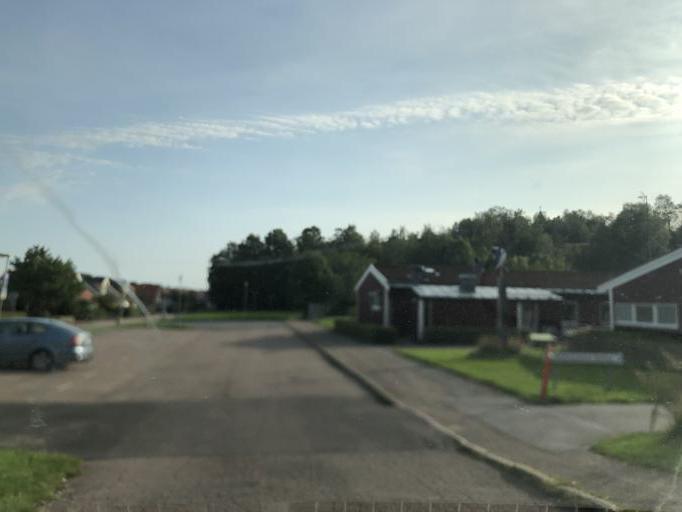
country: SE
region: Vaestra Goetaland
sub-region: Goteborg
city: Goeteborg
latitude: 57.7467
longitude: 11.9845
